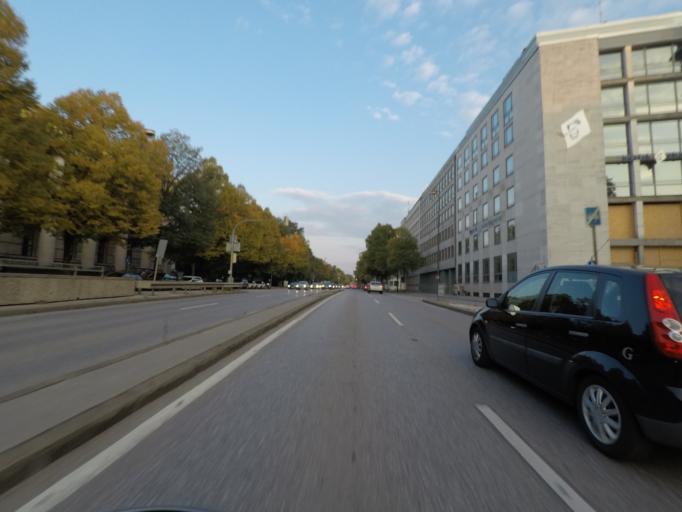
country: DE
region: Bavaria
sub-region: Upper Bavaria
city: Munich
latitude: 48.1437
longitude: 11.5857
